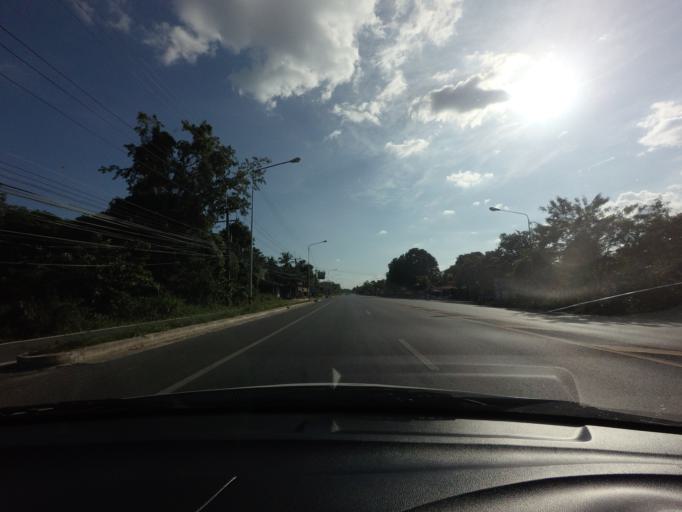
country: TH
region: Nakhon Nayok
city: Nakhon Nayok
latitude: 14.2756
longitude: 101.2745
